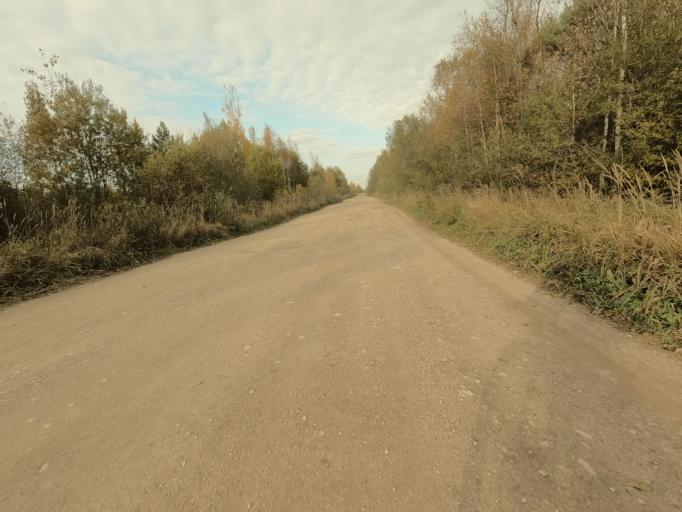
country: RU
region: Novgorod
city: Volkhovskiy
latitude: 58.9092
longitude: 31.0387
